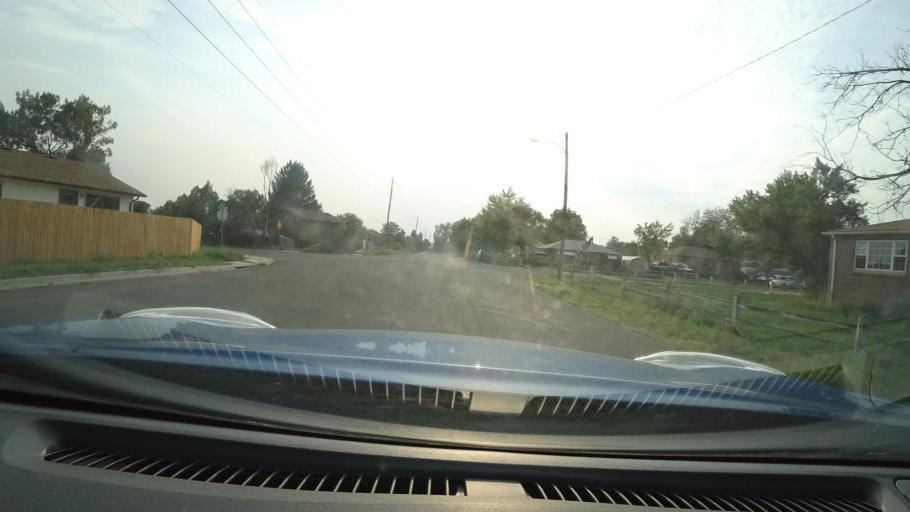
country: US
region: Colorado
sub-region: Adams County
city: Aurora
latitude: 39.7437
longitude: -104.7684
